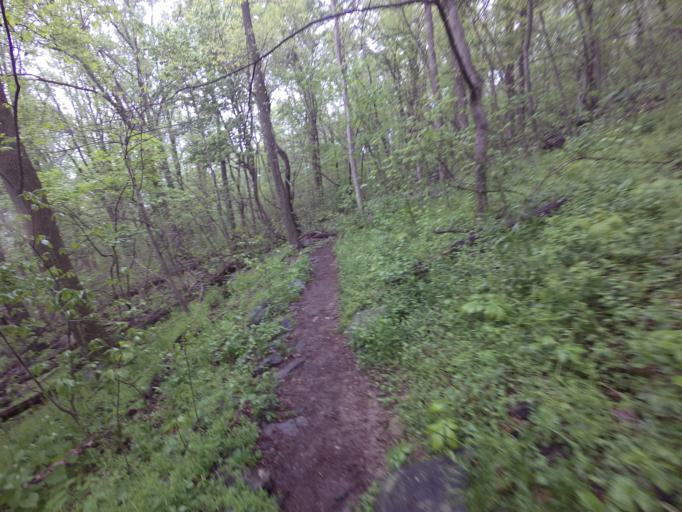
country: US
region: Maryland
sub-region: Frederick County
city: Brunswick
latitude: 39.3322
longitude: -77.6785
